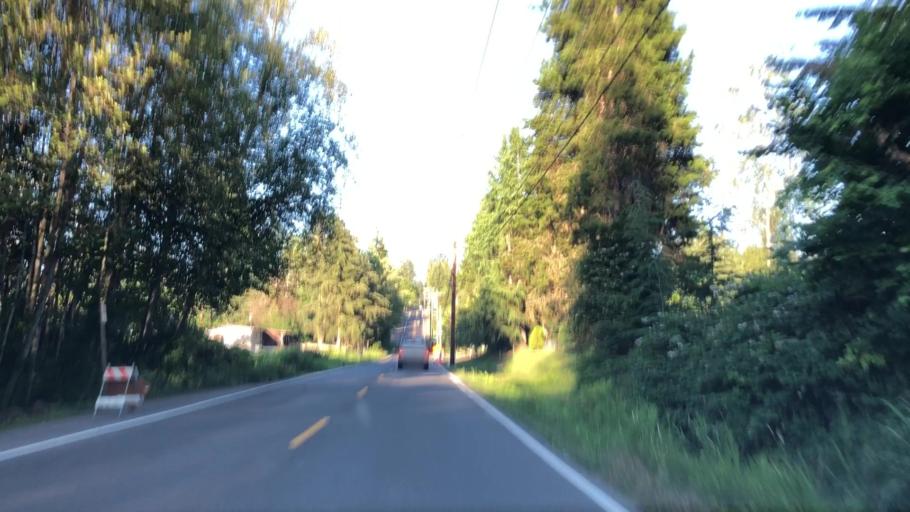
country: US
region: Washington
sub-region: Snohomish County
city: North Creek
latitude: 47.8202
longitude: -122.2051
